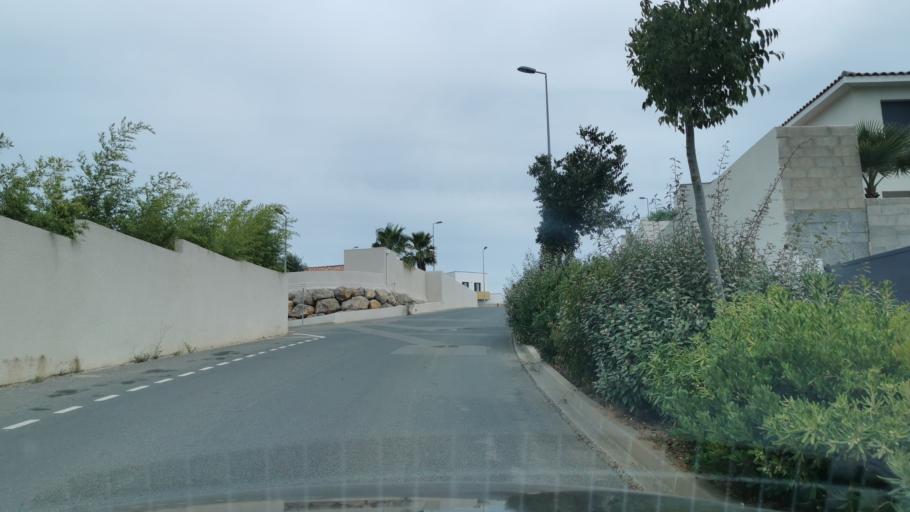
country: FR
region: Languedoc-Roussillon
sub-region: Departement de l'Aude
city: Narbonne
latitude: 43.1954
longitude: 2.9716
